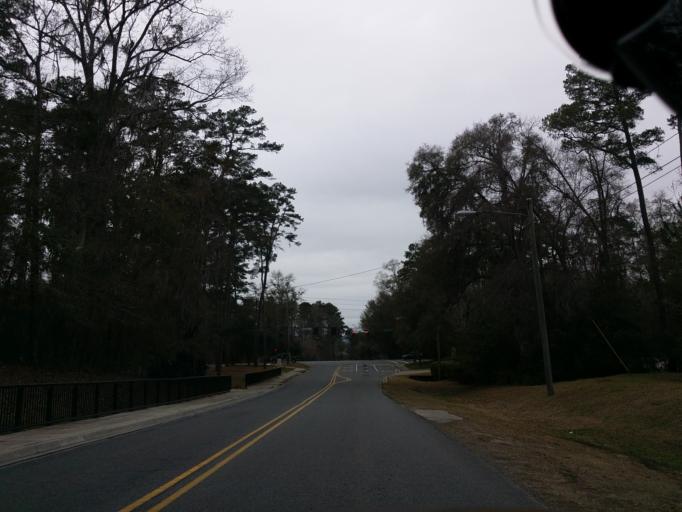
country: US
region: Florida
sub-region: Leon County
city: Tallahassee
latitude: 30.4850
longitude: -84.2277
